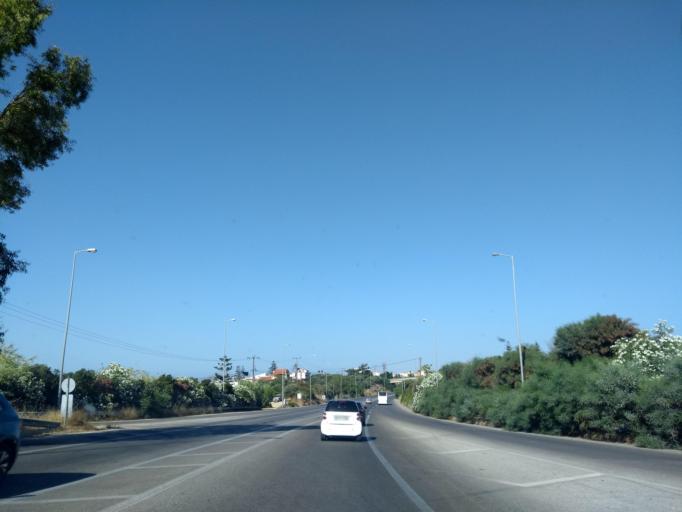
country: GR
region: Crete
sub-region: Nomos Chanias
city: Galatas
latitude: 35.5061
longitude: 23.9641
